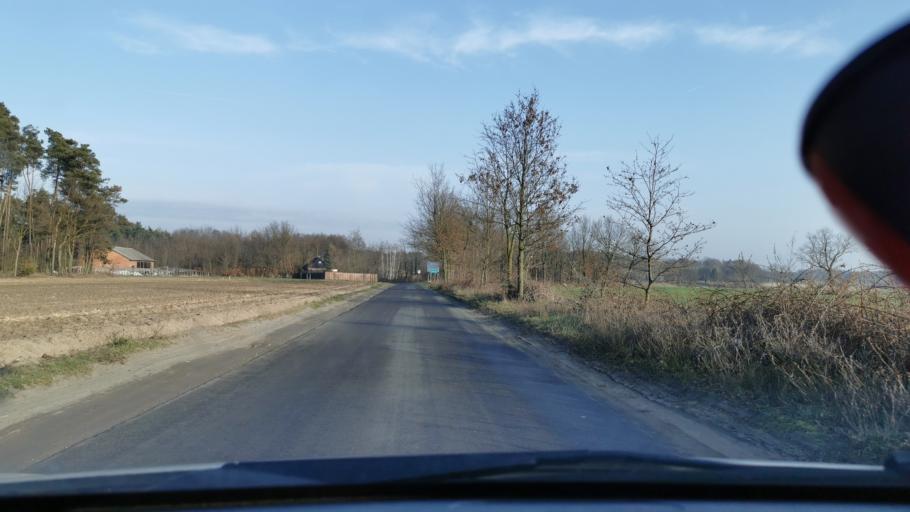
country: PL
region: Greater Poland Voivodeship
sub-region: Powiat kaliski
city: Opatowek
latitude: 51.6587
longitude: 18.2477
